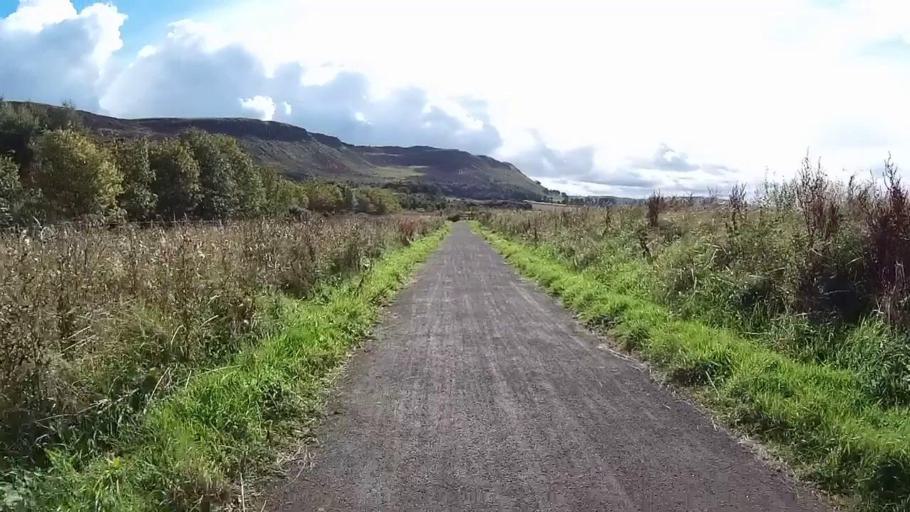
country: GB
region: Scotland
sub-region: Fife
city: Ballingry
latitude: 56.1762
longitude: -3.3566
